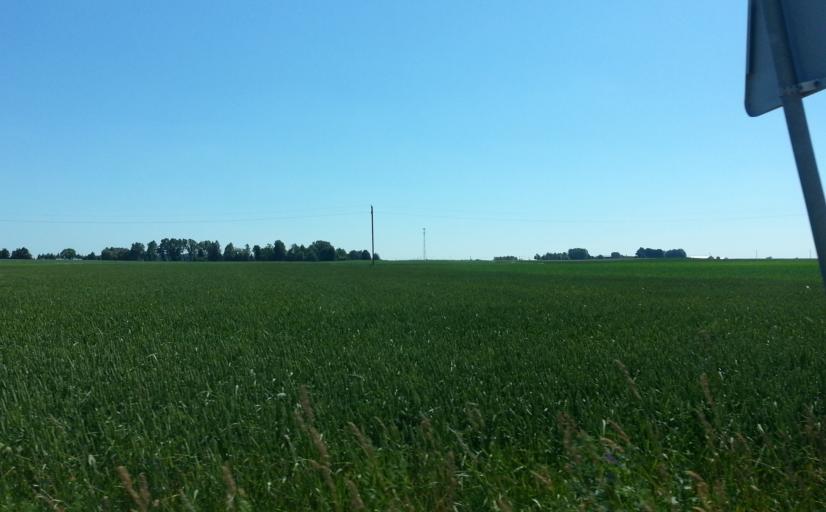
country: LT
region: Panevezys
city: Pasvalys
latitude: 56.2279
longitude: 24.4325
